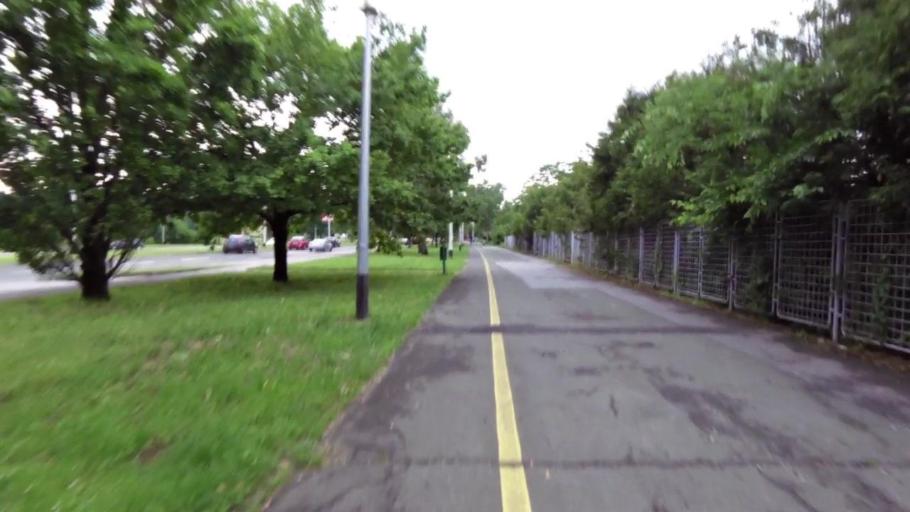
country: HR
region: Grad Zagreb
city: Dubrava
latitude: 45.8290
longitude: 16.0352
